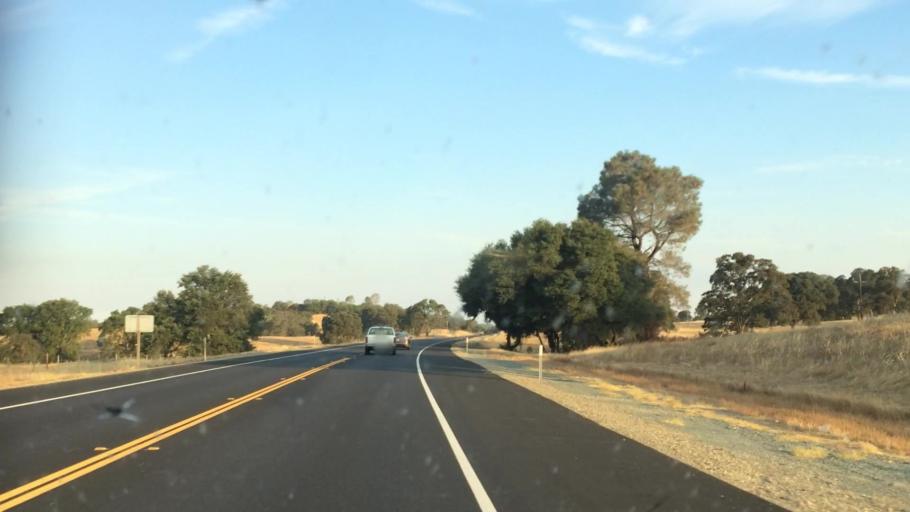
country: US
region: California
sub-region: Amador County
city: Plymouth
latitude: 38.4537
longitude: -120.9194
